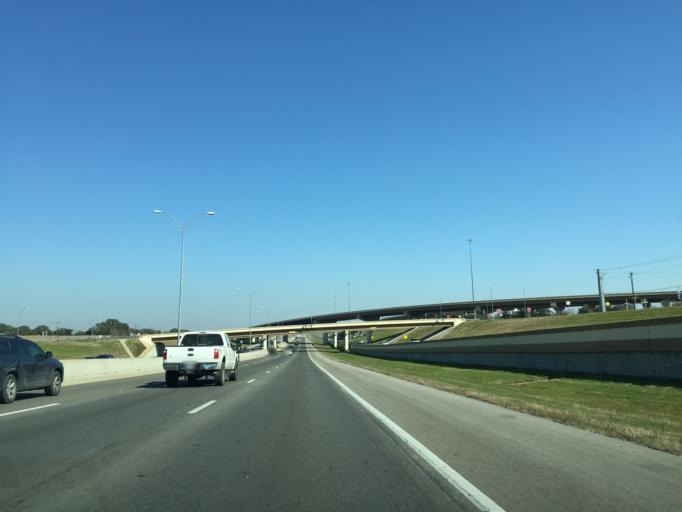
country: US
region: Texas
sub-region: Williamson County
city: Serenada
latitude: 30.6834
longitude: -97.6590
